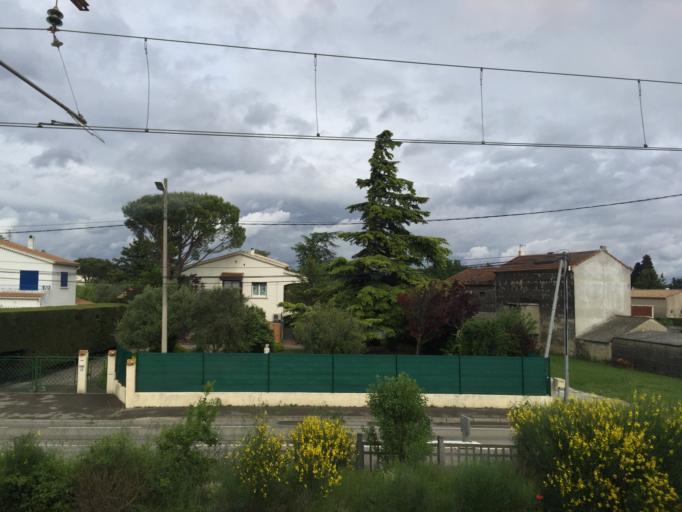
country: FR
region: Rhone-Alpes
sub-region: Departement de la Drome
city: Pierrelatte
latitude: 44.3809
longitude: 4.7048
